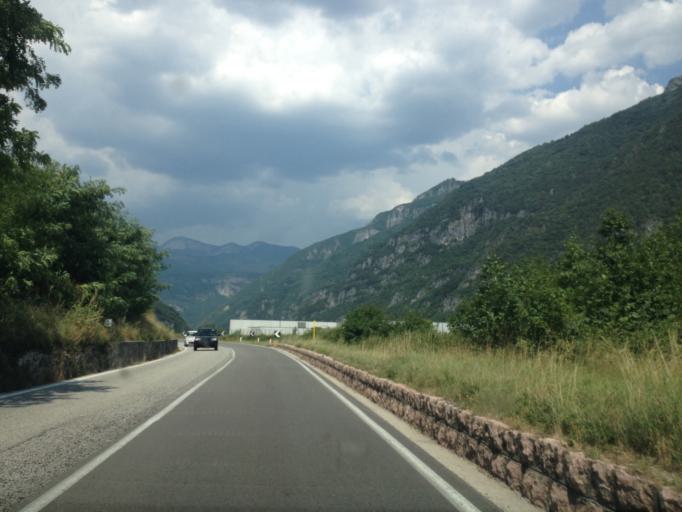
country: IT
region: Veneto
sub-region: Provincia di Vicenza
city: Arsiero
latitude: 45.8133
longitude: 11.3631
